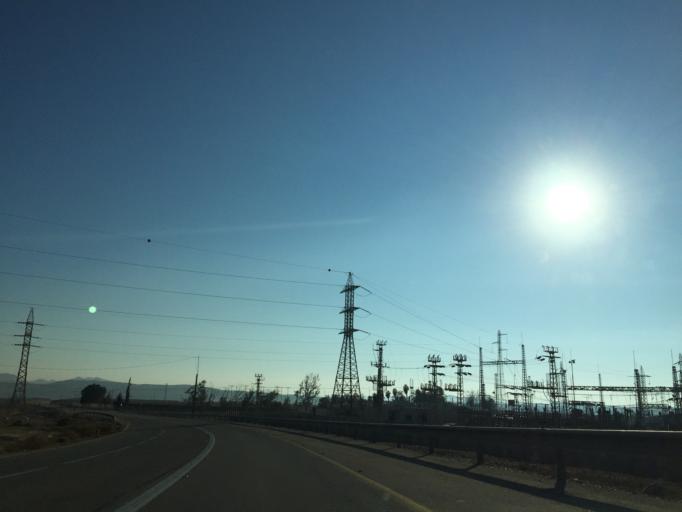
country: IL
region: Southern District
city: Mitzpe Ramon
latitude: 30.2894
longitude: 34.9858
